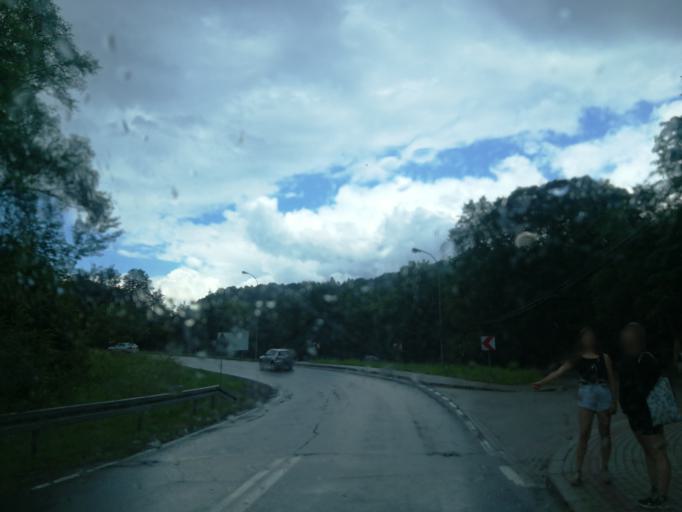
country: PL
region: Subcarpathian Voivodeship
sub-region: Powiat leski
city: Polanczyk
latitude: 49.4010
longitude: 22.4597
